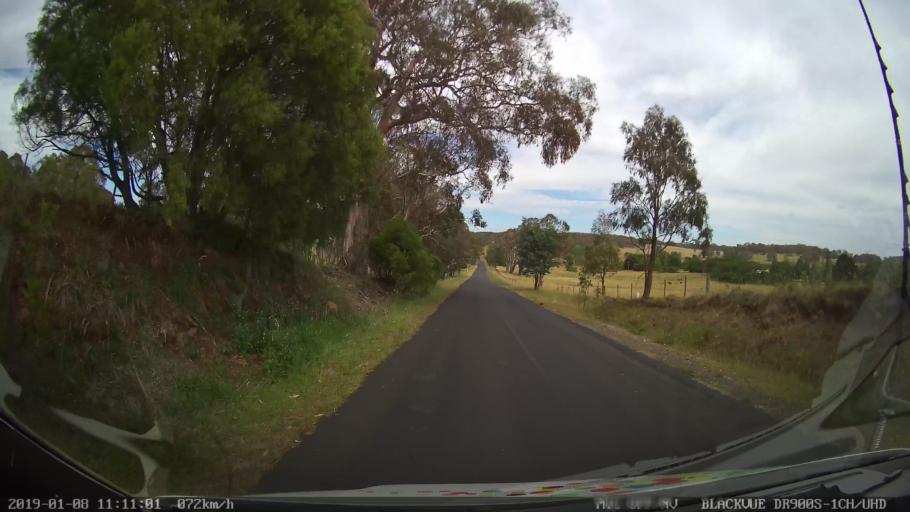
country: AU
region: New South Wales
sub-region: Guyra
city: Guyra
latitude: -30.2266
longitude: 151.6297
